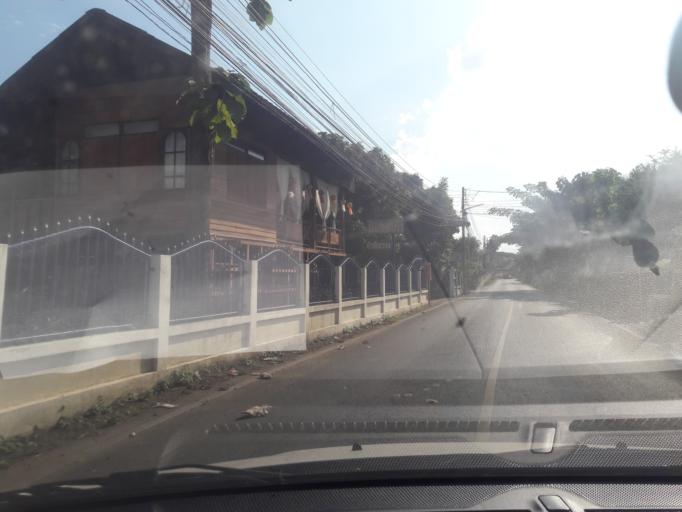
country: TH
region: Chiang Mai
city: San Kamphaeng
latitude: 18.7557
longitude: 99.1413
